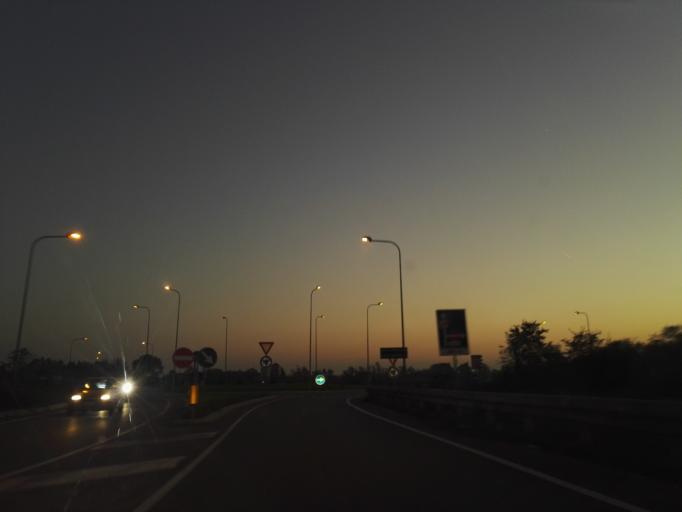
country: IT
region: Lombardy
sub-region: Citta metropolitana di Milano
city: San Bovio-San Felice
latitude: 45.4664
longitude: 9.3026
